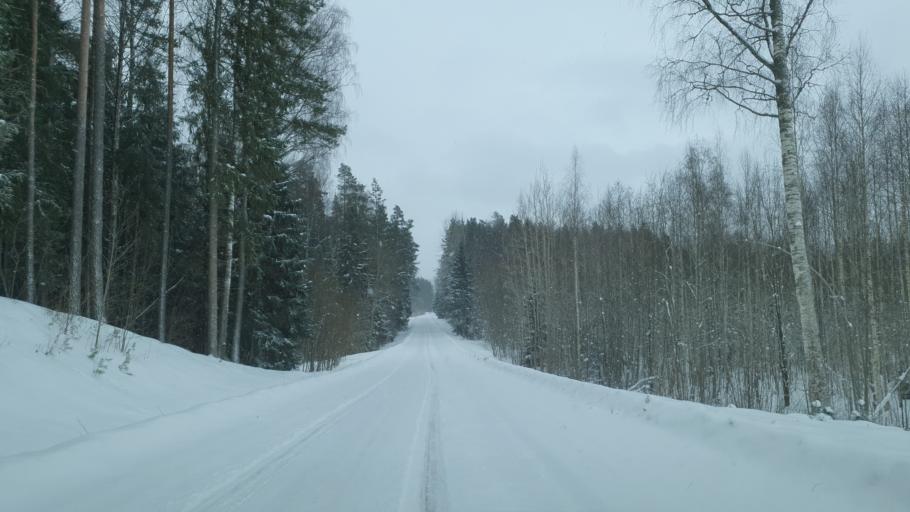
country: EE
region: Tartu
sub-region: Tartu linn
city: Tartu
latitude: 58.5614
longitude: 26.8506
